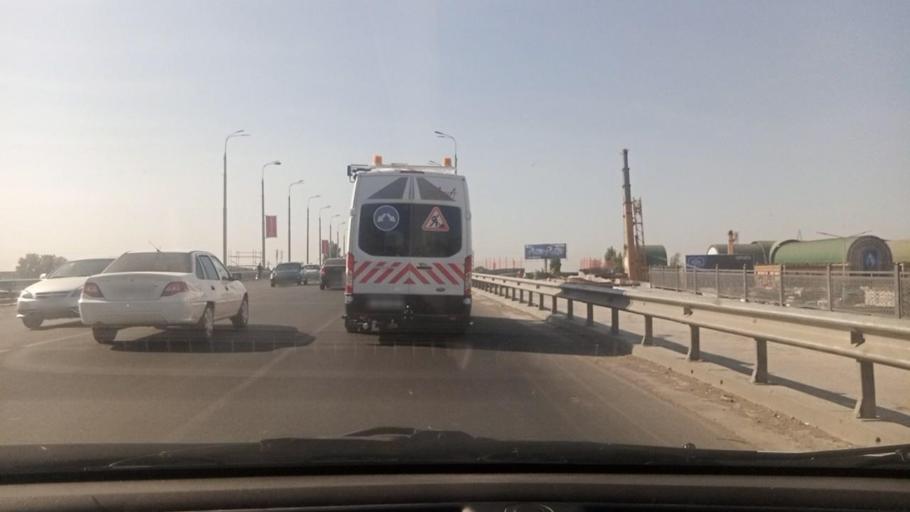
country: UZ
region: Toshkent Shahri
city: Bektemir
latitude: 41.2392
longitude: 69.3301
